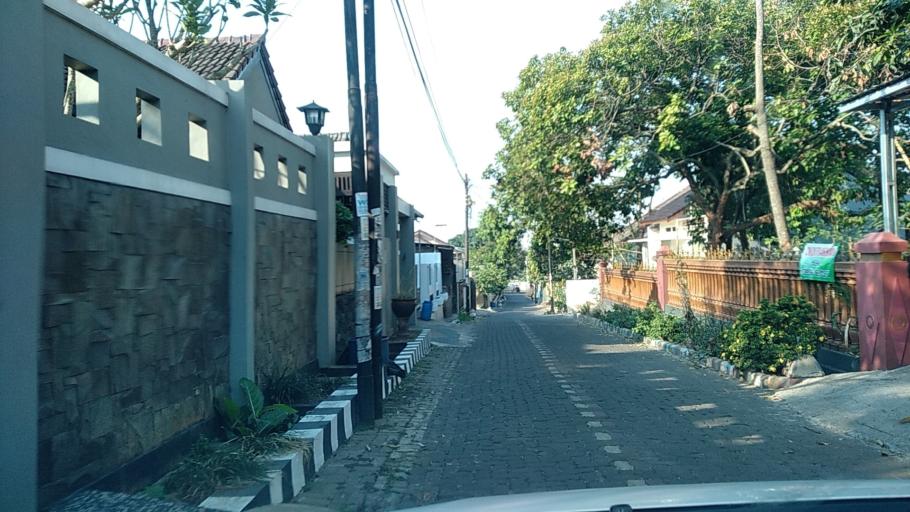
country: ID
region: Central Java
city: Semarang
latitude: -7.0670
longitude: 110.4289
